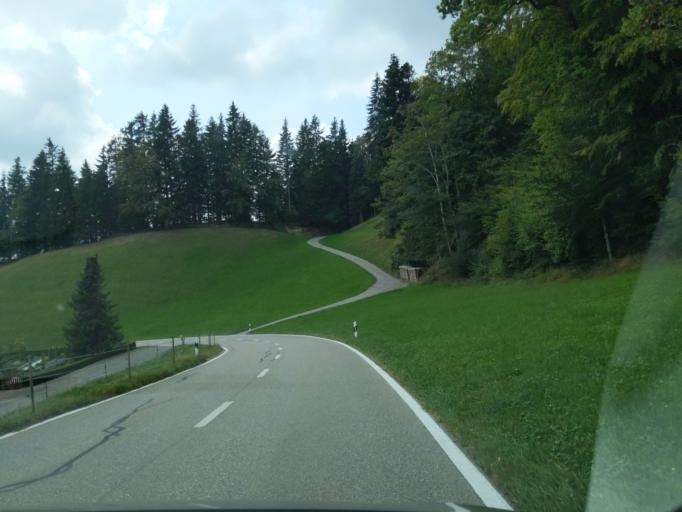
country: CH
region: Bern
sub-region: Oberaargau
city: Wyssachen
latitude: 47.0546
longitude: 7.8350
